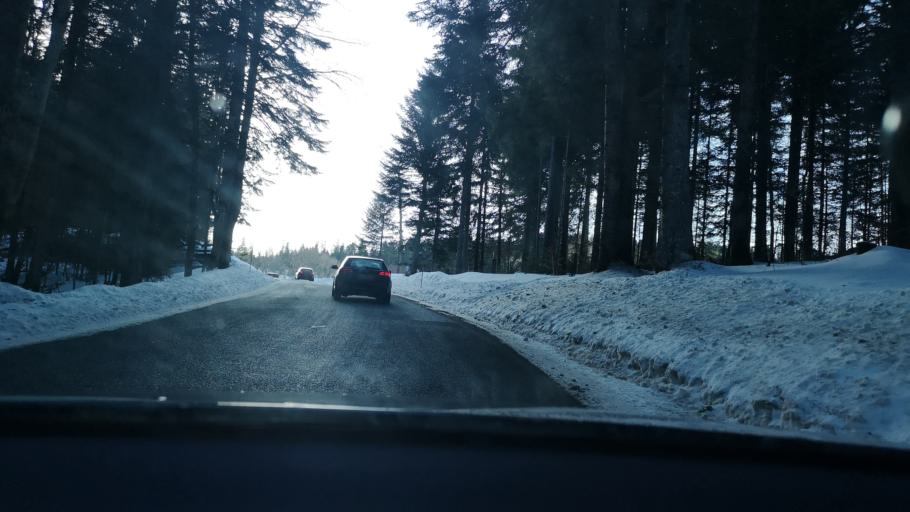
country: FR
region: Franche-Comte
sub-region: Departement du Doubs
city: Gilley
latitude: 46.9917
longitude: 6.5267
